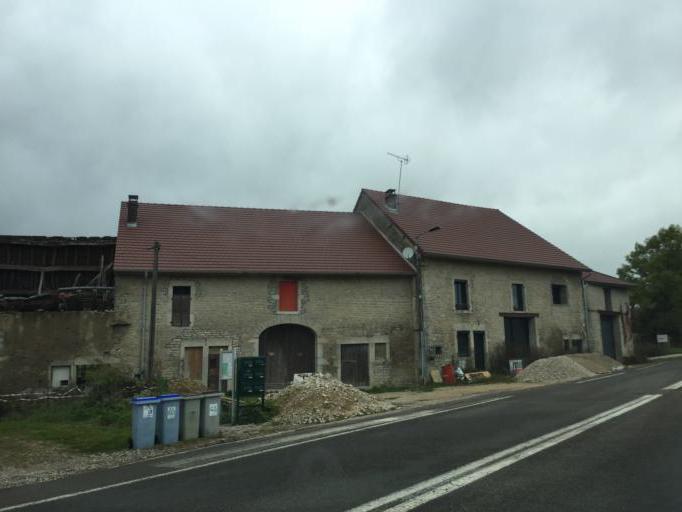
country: FR
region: Franche-Comte
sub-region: Departement du Jura
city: Orgelet
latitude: 46.5447
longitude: 5.5996
